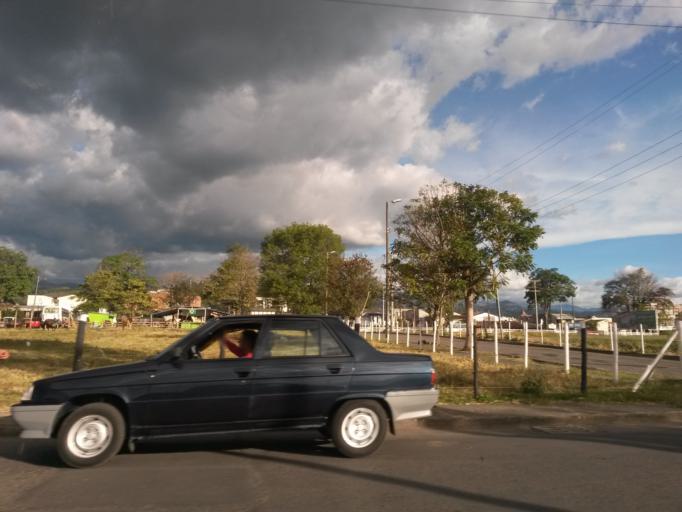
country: CO
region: Cauca
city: Popayan
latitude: 2.4553
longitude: -76.6003
